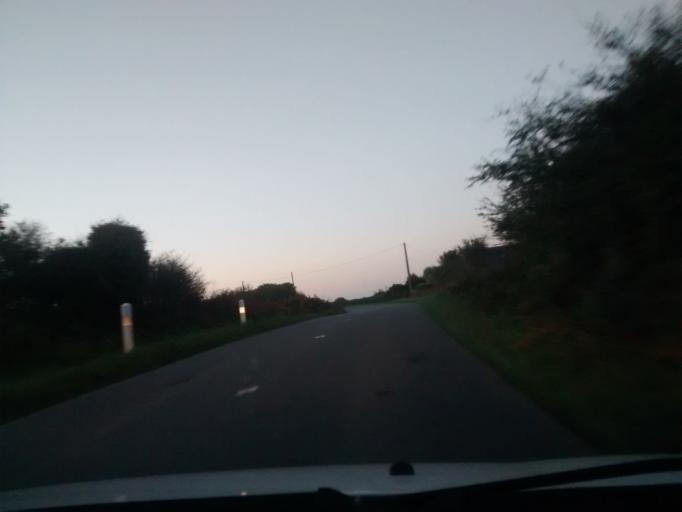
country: FR
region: Brittany
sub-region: Departement des Cotes-d'Armor
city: Trevou-Treguignec
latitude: 48.8080
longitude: -3.3288
